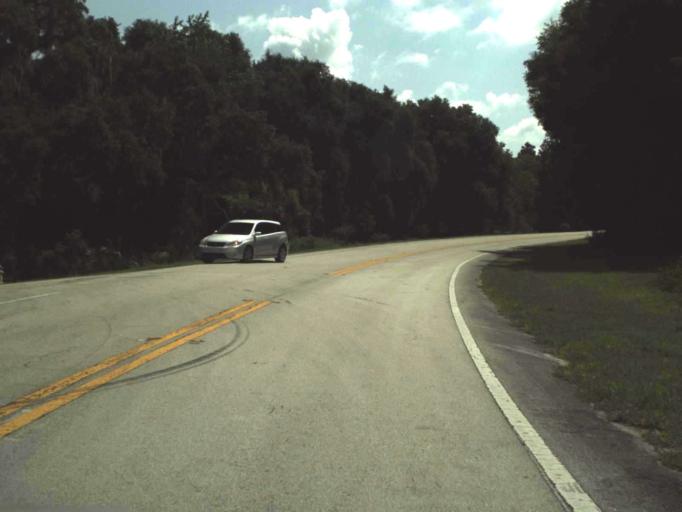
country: US
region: Florida
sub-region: Volusia County
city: Lake Helen
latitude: 29.0172
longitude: -81.2443
